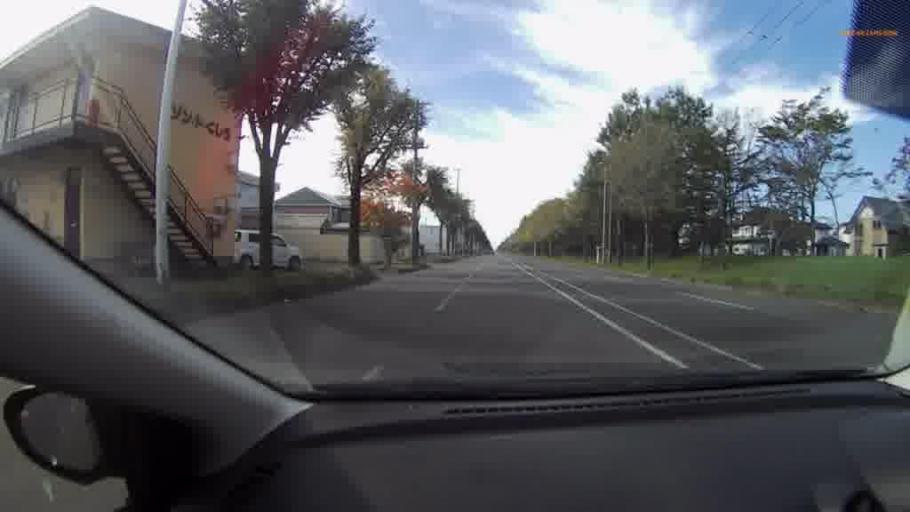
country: JP
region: Hokkaido
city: Kushiro
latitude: 43.0213
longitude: 144.4166
